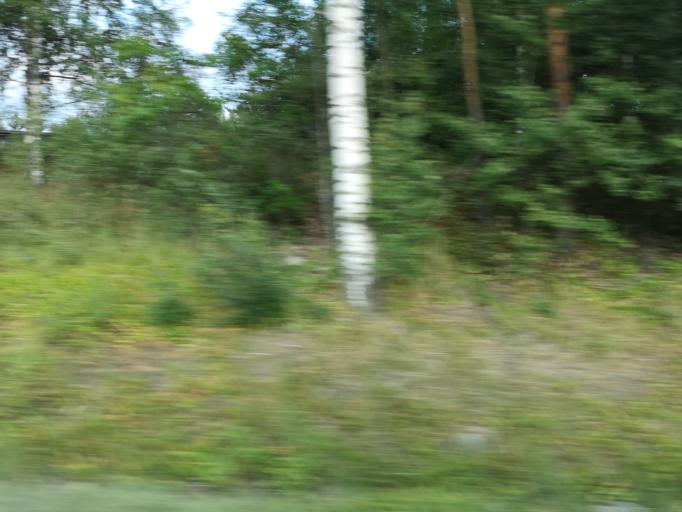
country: FI
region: Paijanne Tavastia
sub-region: Lahti
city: Hartola
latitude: 61.6221
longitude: 26.0104
